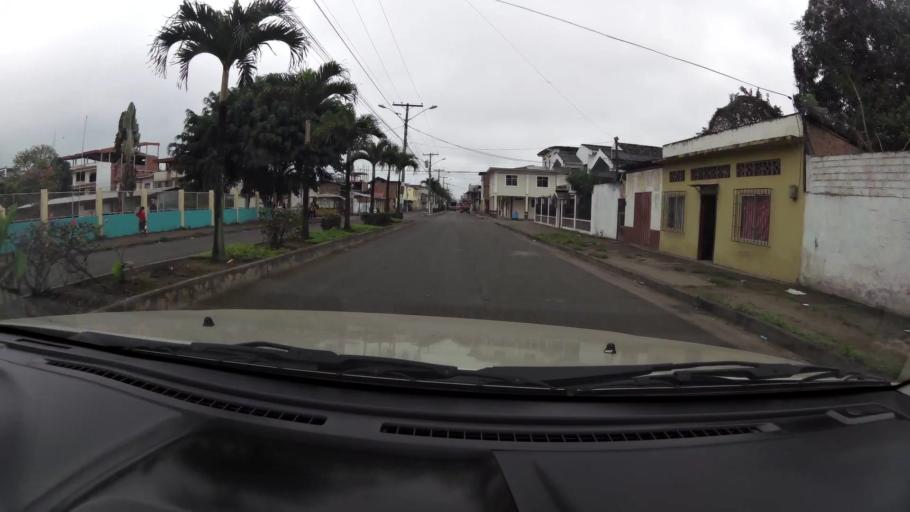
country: EC
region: El Oro
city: Pasaje
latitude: -3.3241
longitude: -79.8026
